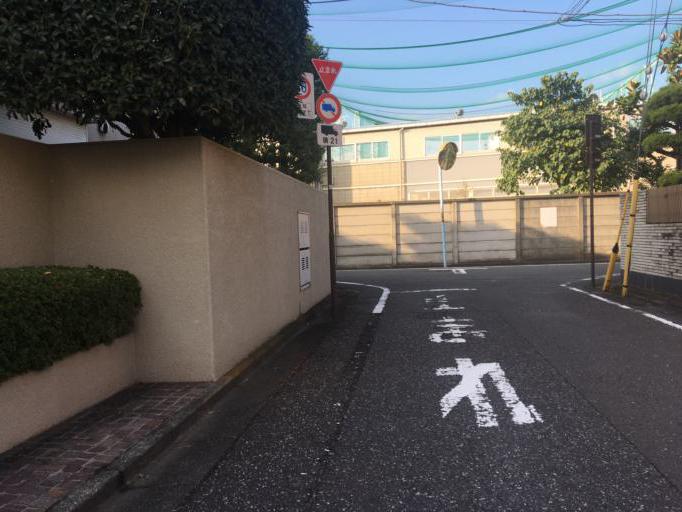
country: JP
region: Tokyo
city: Musashino
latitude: 35.7235
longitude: 139.5993
